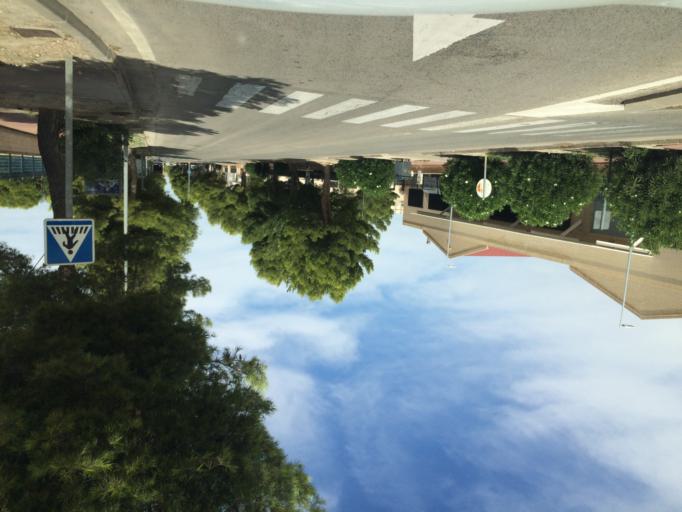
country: ES
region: Castille-La Mancha
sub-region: Provincia de Albacete
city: Albacete
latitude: 39.0180
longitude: -1.8824
